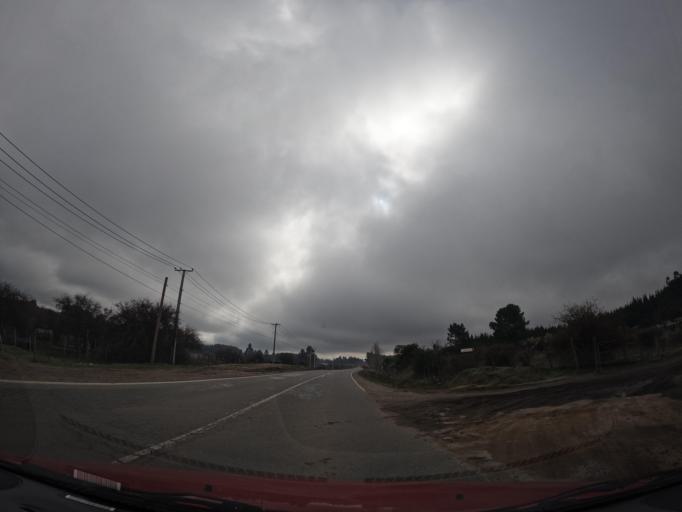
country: CL
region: Maule
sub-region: Provincia de Cauquenes
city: Cauquenes
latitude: -36.2666
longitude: -72.5479
